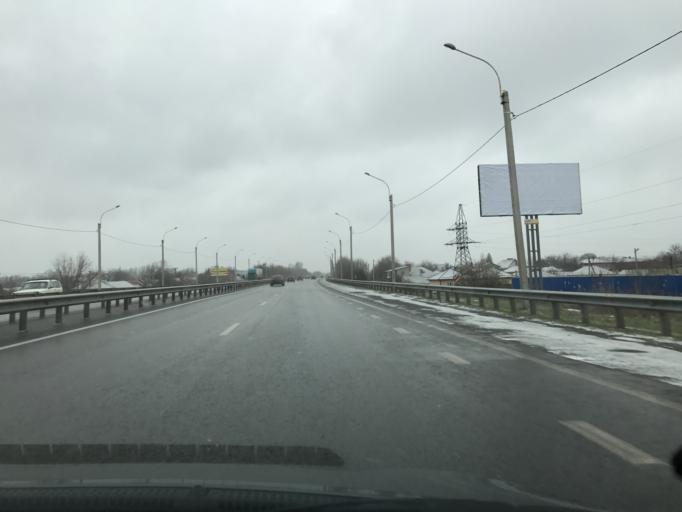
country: RU
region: Rostov
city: Bataysk
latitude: 47.1356
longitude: 39.7761
